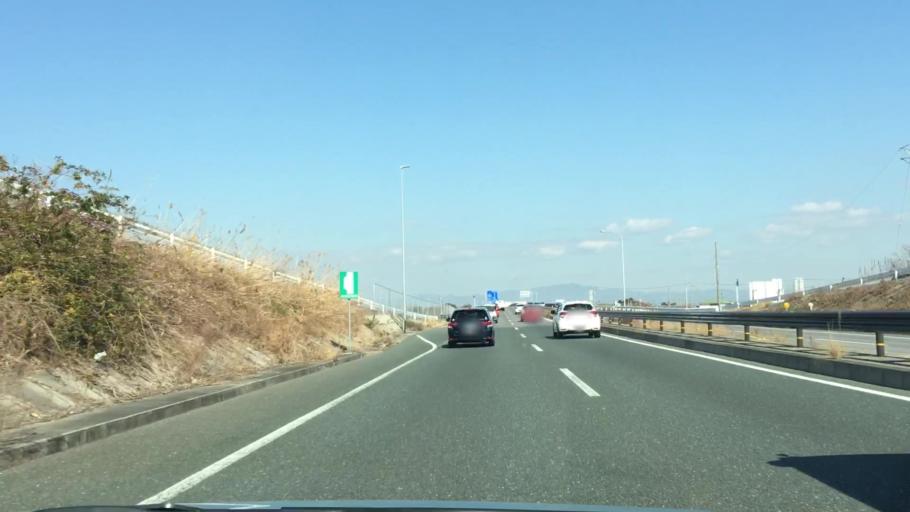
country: JP
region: Aichi
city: Toyohashi
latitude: 34.7165
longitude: 137.3526
